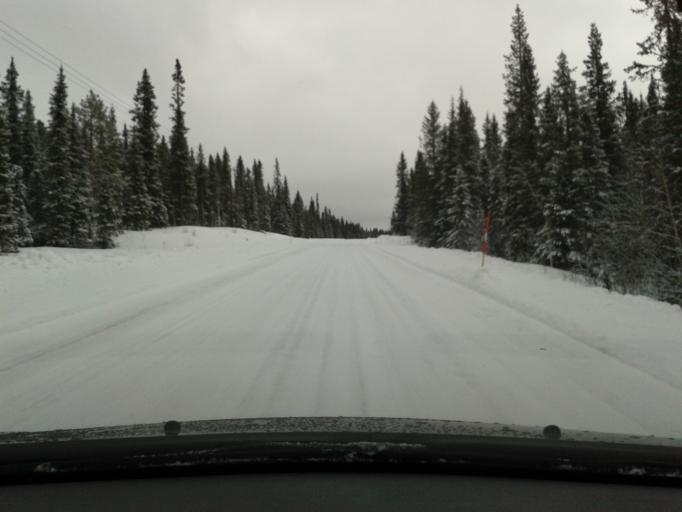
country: SE
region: Vaesterbotten
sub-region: Vilhelmina Kommun
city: Sjoberg
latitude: 65.2373
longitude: 15.8220
